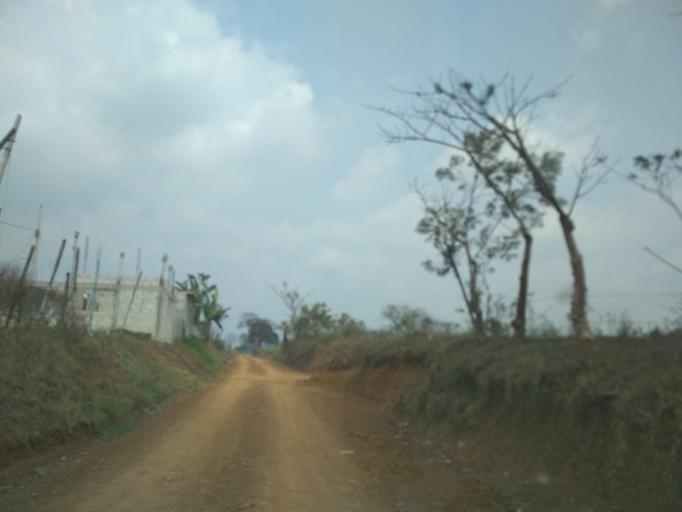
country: MX
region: Veracruz
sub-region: Cordoba
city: Fredepo
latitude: 18.8598
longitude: -96.9807
